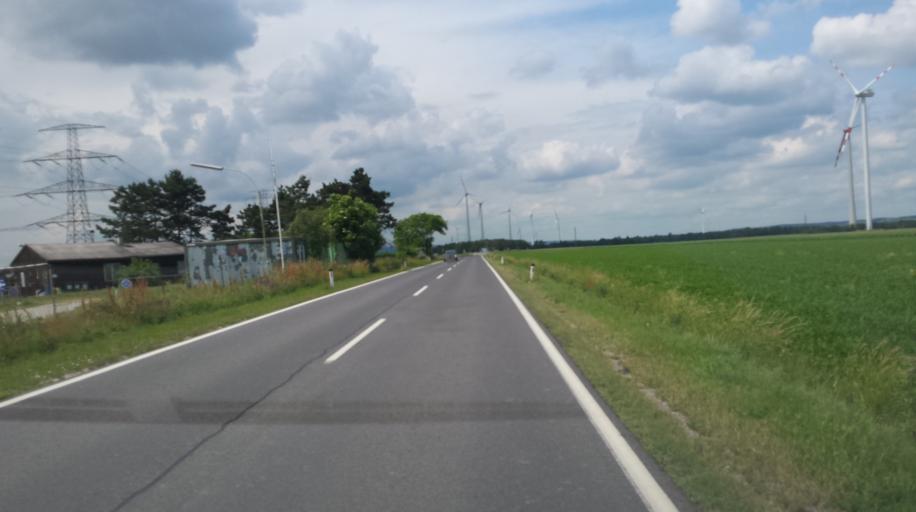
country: AT
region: Lower Austria
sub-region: Politischer Bezirk Mistelbach
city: Pillichsdorf
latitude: 48.3173
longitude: 16.5326
